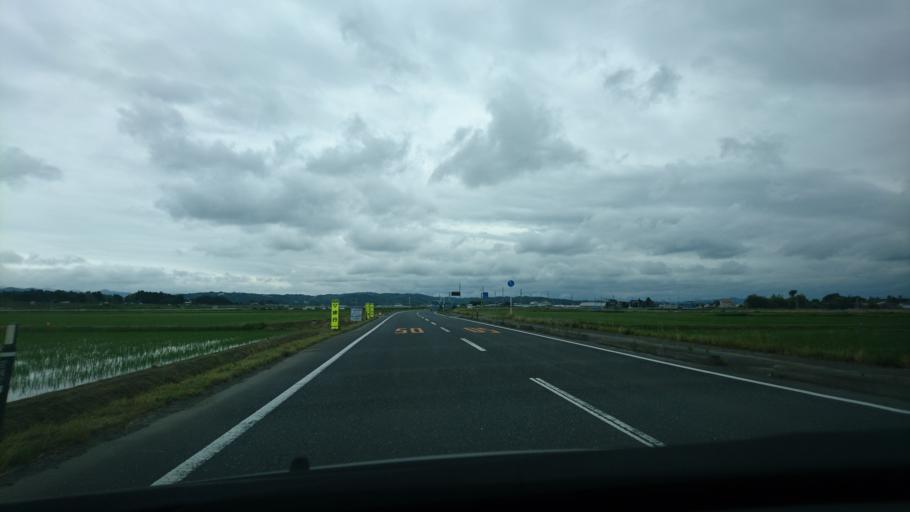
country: JP
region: Miyagi
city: Wakuya
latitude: 38.6811
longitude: 141.2611
